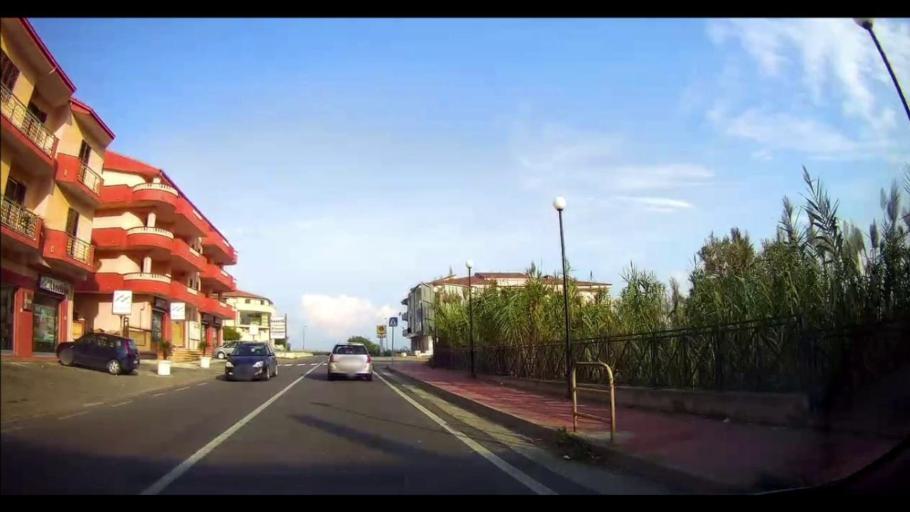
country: IT
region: Calabria
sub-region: Provincia di Cosenza
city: Cariati
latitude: 39.5062
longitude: 16.9367
